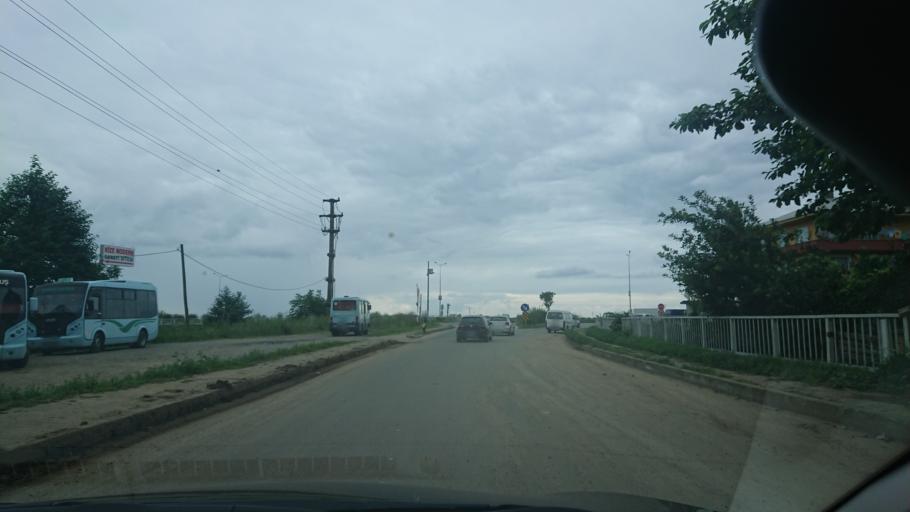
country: TR
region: Rize
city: Rize
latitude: 41.0342
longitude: 40.4803
